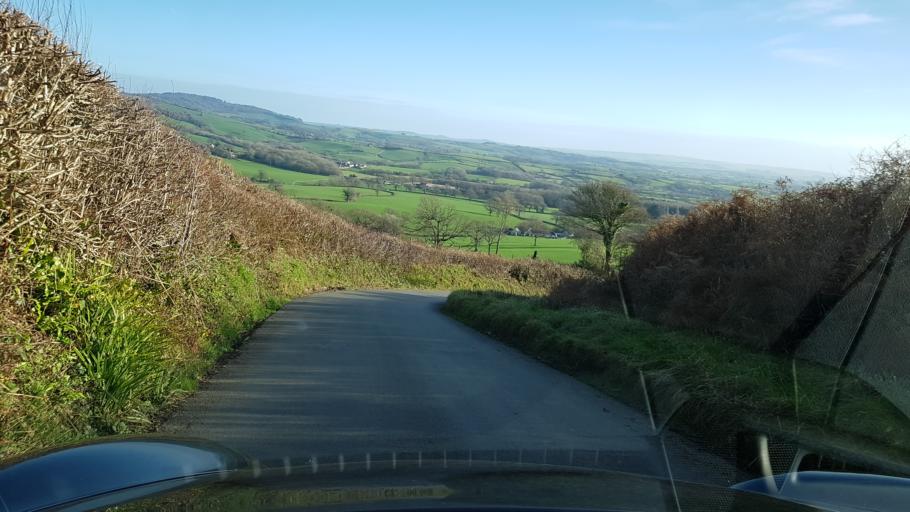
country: GB
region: England
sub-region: Dorset
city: Lyme Regis
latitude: 50.7924
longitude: -2.8724
